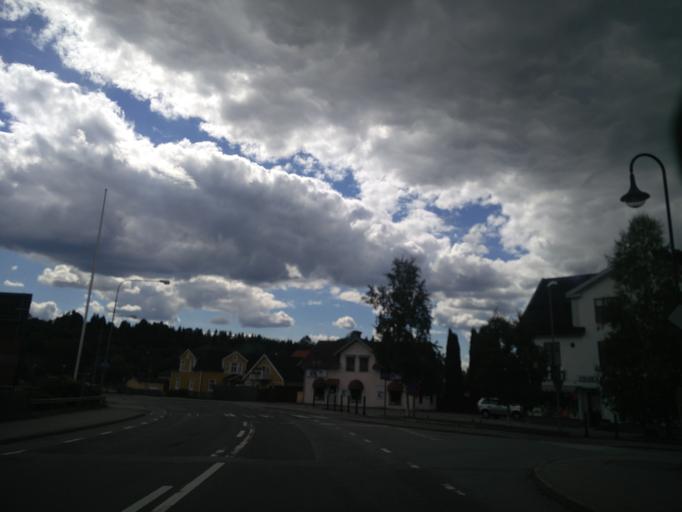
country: SE
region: OErebro
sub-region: Ljusnarsbergs Kommun
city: Kopparberg
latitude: 59.8748
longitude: 14.9880
